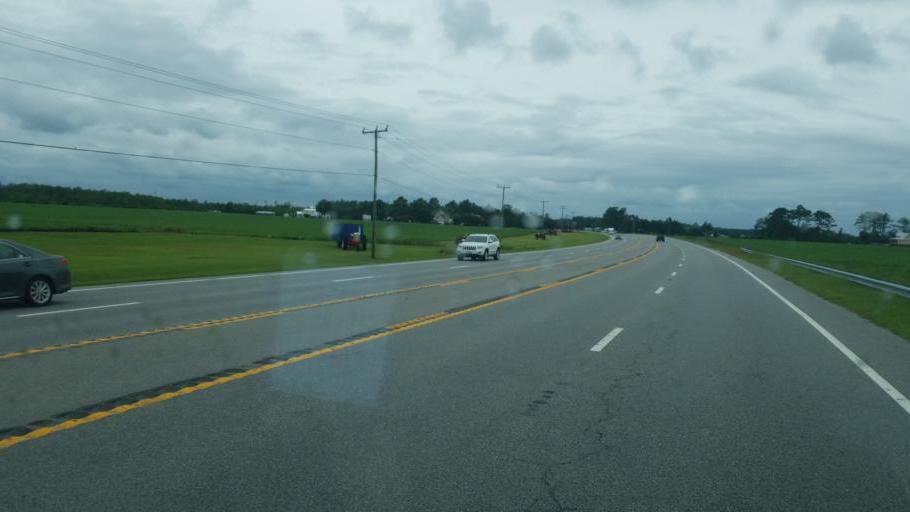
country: US
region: North Carolina
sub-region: Currituck County
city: Currituck
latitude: 36.3997
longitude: -75.9855
